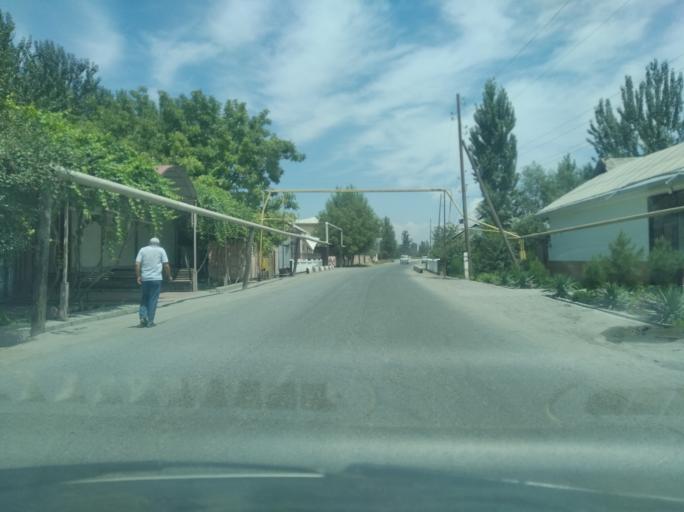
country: UZ
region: Andijon
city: Khujaobod
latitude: 40.6363
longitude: 72.4491
